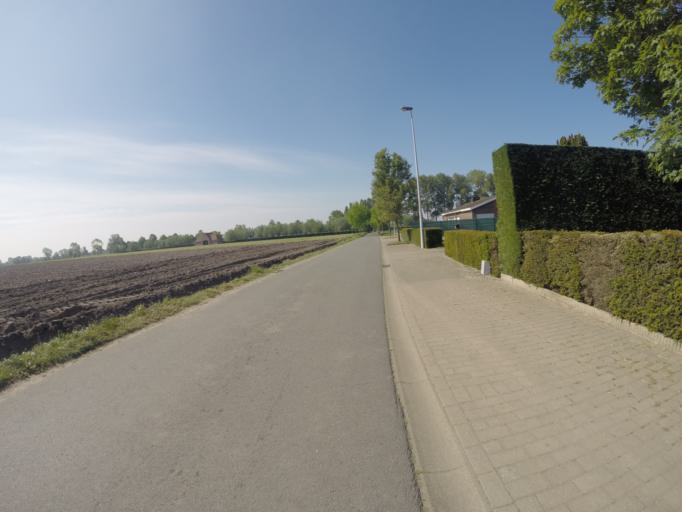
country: BE
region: Flanders
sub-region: Provincie West-Vlaanderen
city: Beernem
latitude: 51.1640
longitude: 3.3559
